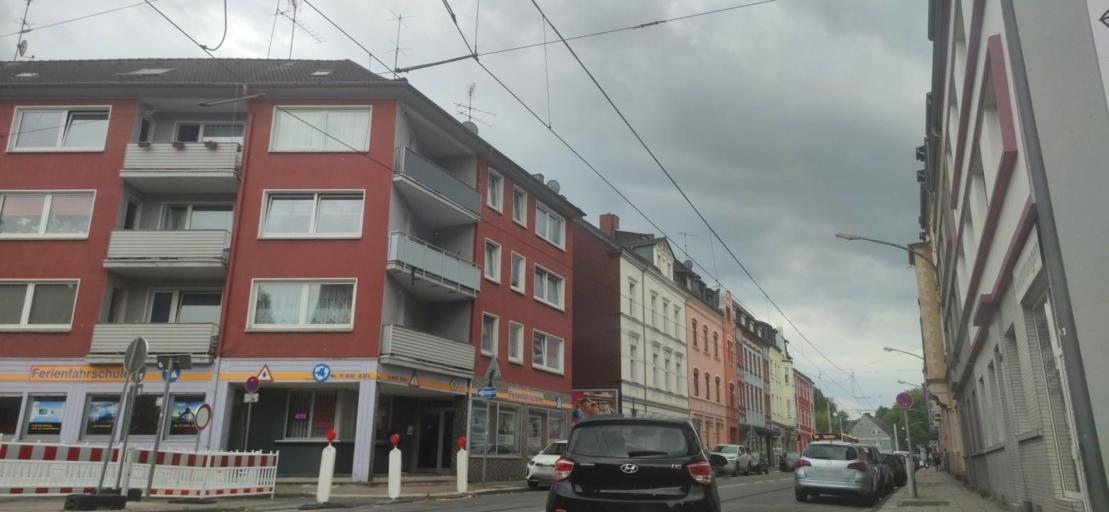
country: DE
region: North Rhine-Westphalia
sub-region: Regierungsbezirk Dusseldorf
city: Essen
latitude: 51.4920
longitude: 7.0494
